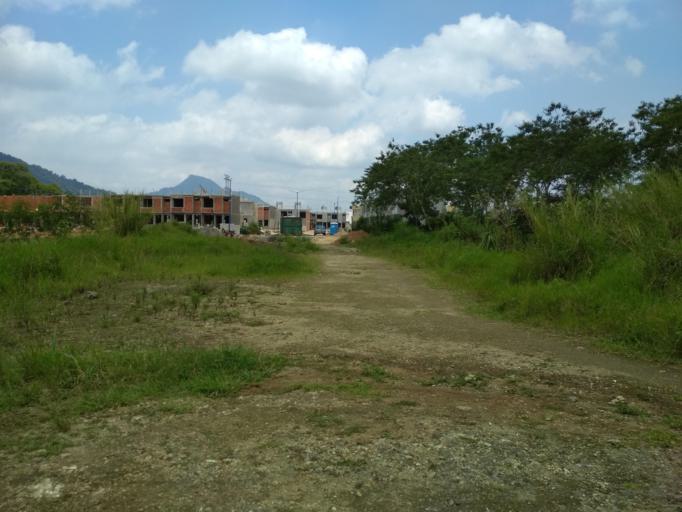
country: MX
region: Veracruz
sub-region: Ixtaczoquitlan
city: Buenavista
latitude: 18.8844
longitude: -97.0610
